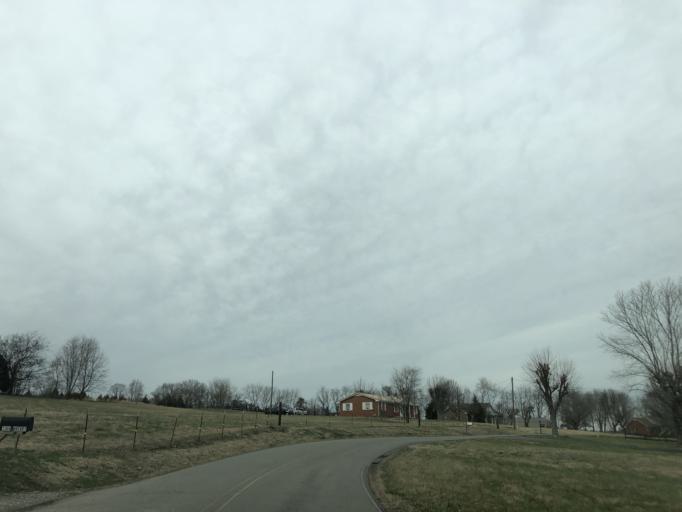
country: US
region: Tennessee
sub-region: Robertson County
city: Greenbrier
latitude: 36.4799
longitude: -86.7967
